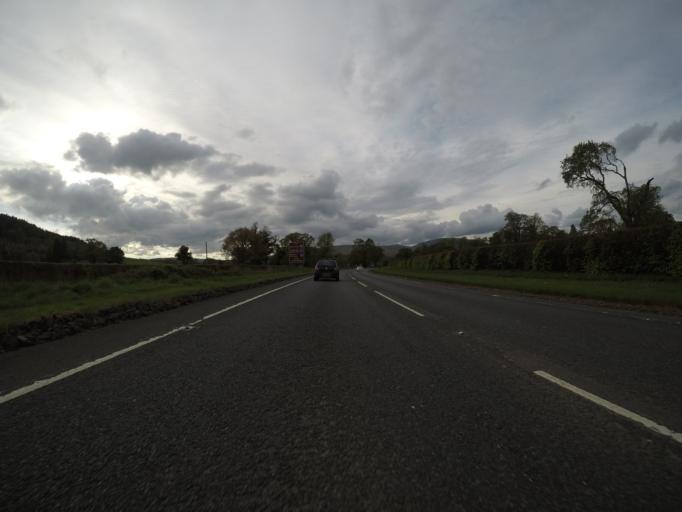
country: GB
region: Scotland
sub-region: West Dunbartonshire
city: Balloch
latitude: 56.0225
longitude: -4.6303
